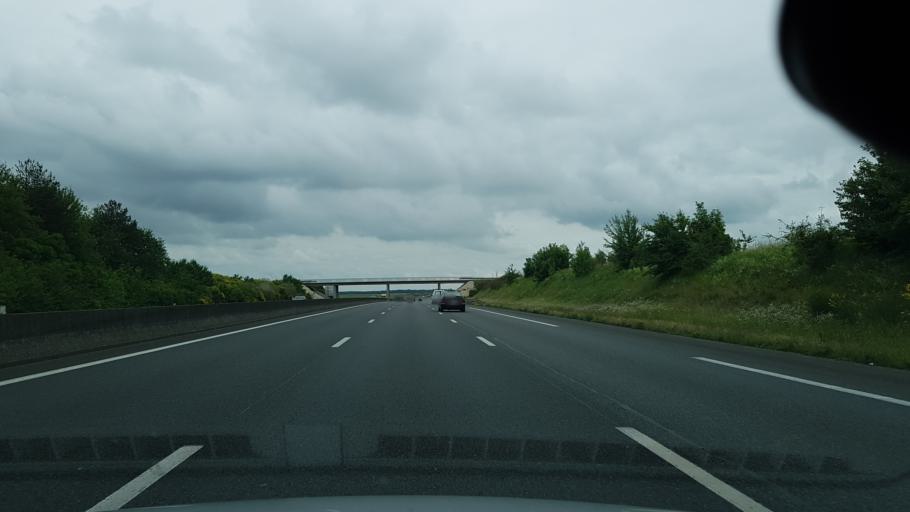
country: FR
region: Centre
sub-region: Departement du Loir-et-Cher
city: Suevres
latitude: 47.6970
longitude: 1.4409
